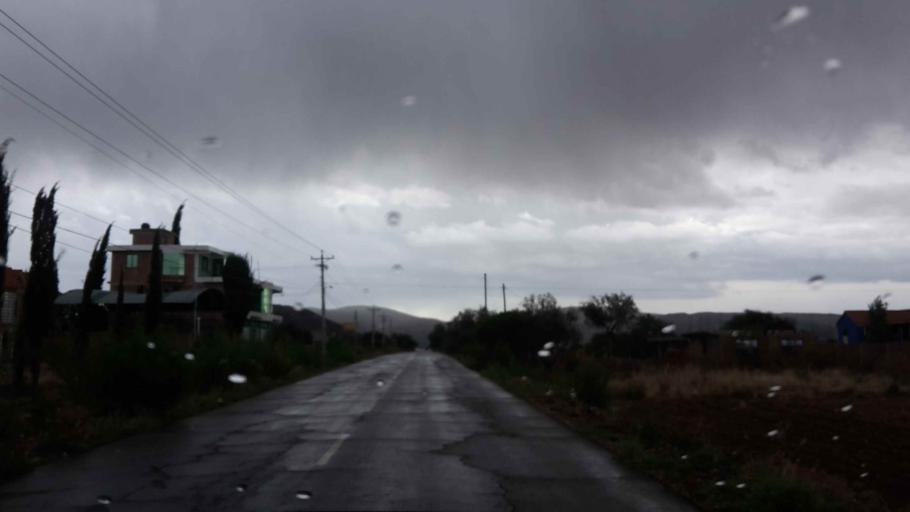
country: BO
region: Cochabamba
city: Tarata
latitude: -17.5602
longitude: -66.0826
